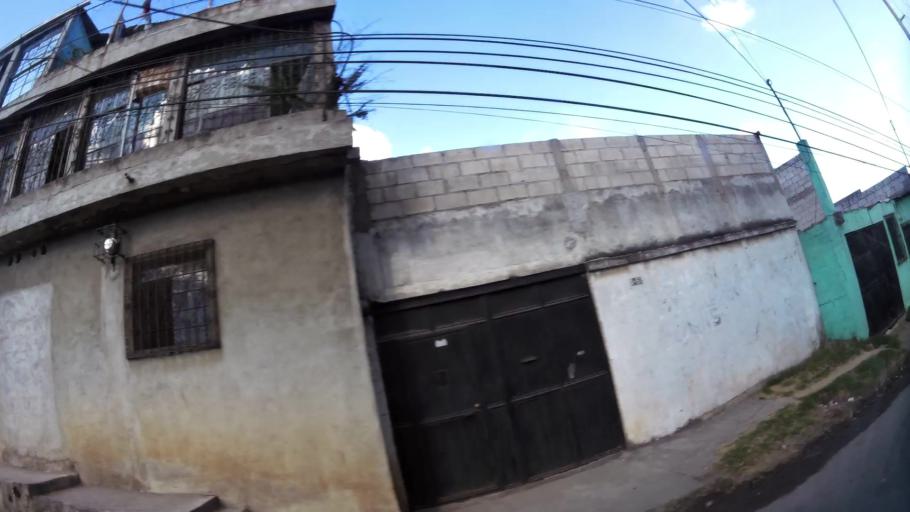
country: GT
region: Guatemala
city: Villa Nueva
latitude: 14.5312
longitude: -90.5922
